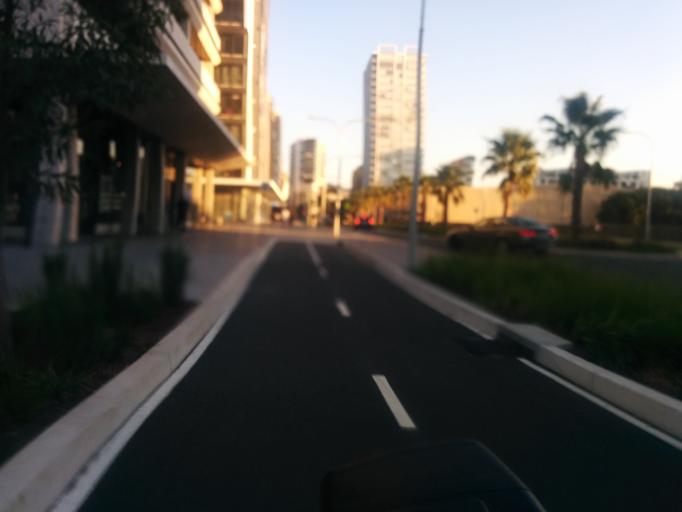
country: AU
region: New South Wales
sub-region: City of Sydney
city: Redfern
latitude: -33.9017
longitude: 151.2131
